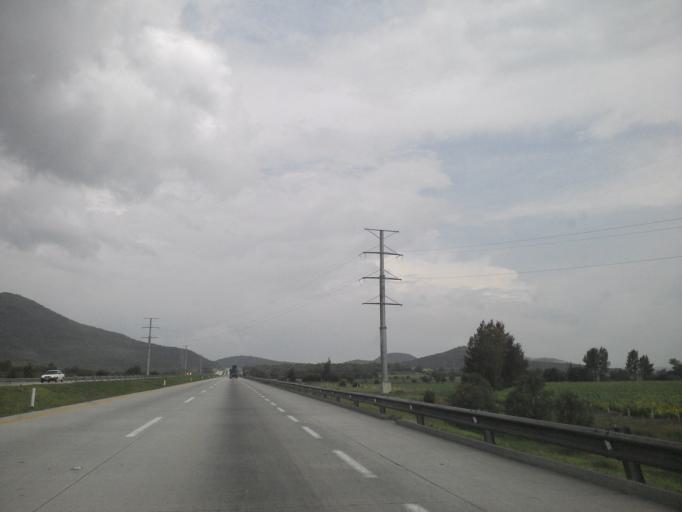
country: MX
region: Hidalgo
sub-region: Atitalaquia
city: Tezoquipa
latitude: 20.0451
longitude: -99.1847
